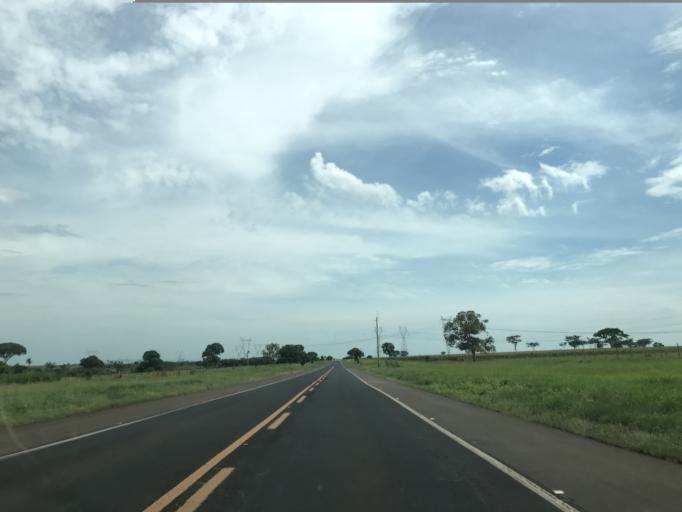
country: BR
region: Sao Paulo
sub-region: Nova Granada
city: Nova Granada
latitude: -20.3426
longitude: -49.2154
